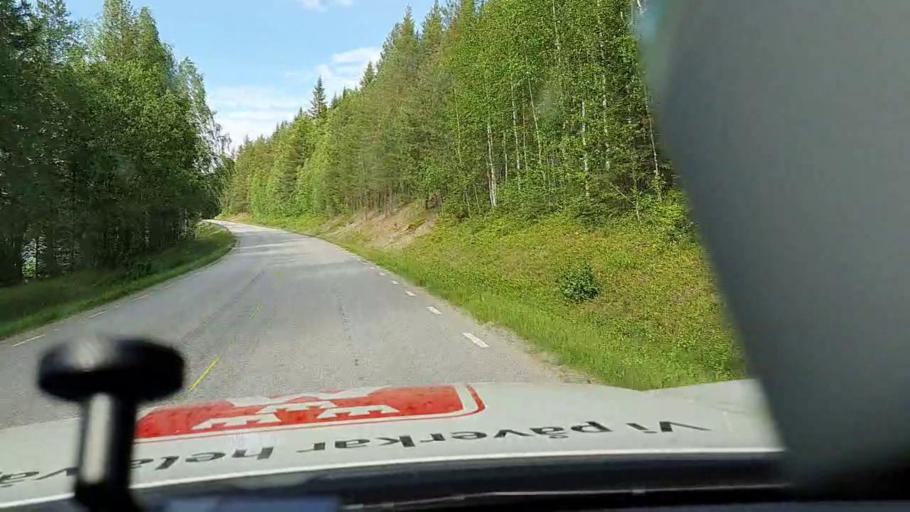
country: SE
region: Norrbotten
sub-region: Gallivare Kommun
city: Gaellivare
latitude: 66.4459
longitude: 20.6517
